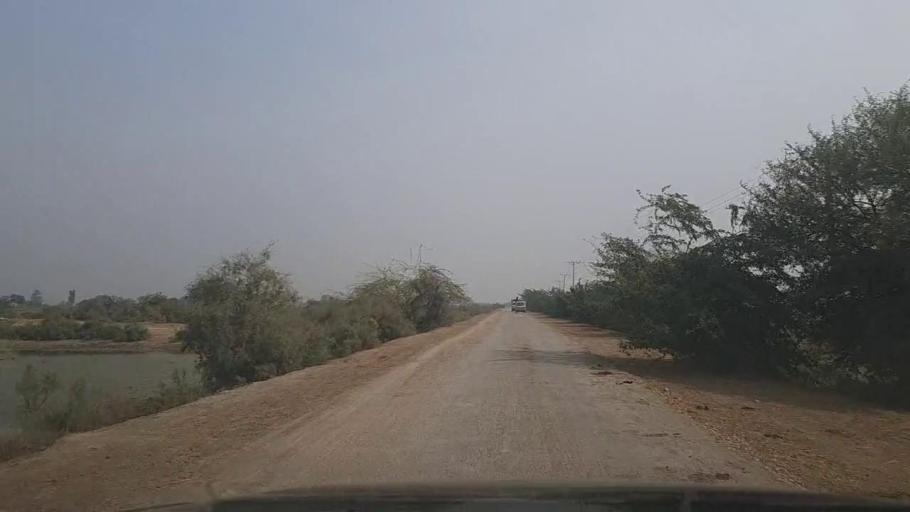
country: PK
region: Sindh
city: Mirpur Sakro
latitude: 24.4793
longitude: 67.6500
